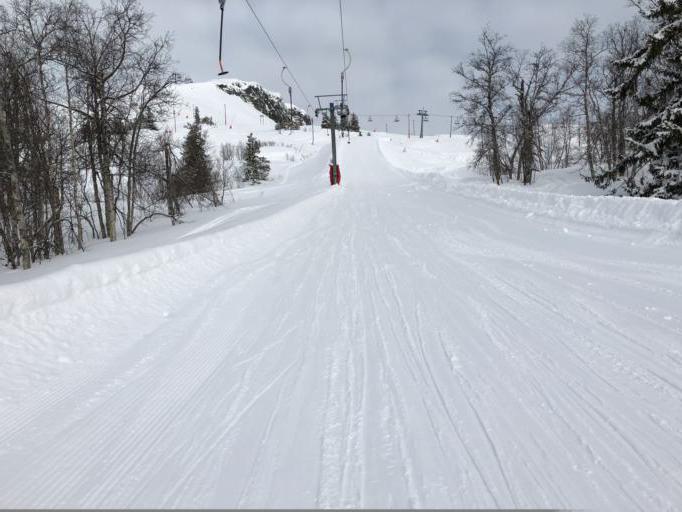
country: NO
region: Oppland
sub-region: Gausdal
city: Segalstad bru
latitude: 61.3422
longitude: 10.0876
